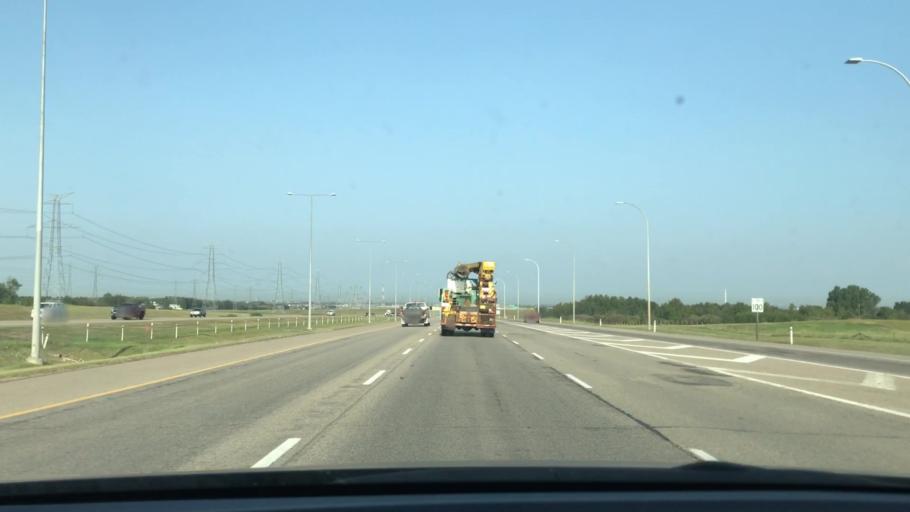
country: CA
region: Alberta
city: Beaumont
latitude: 53.4357
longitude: -113.4238
